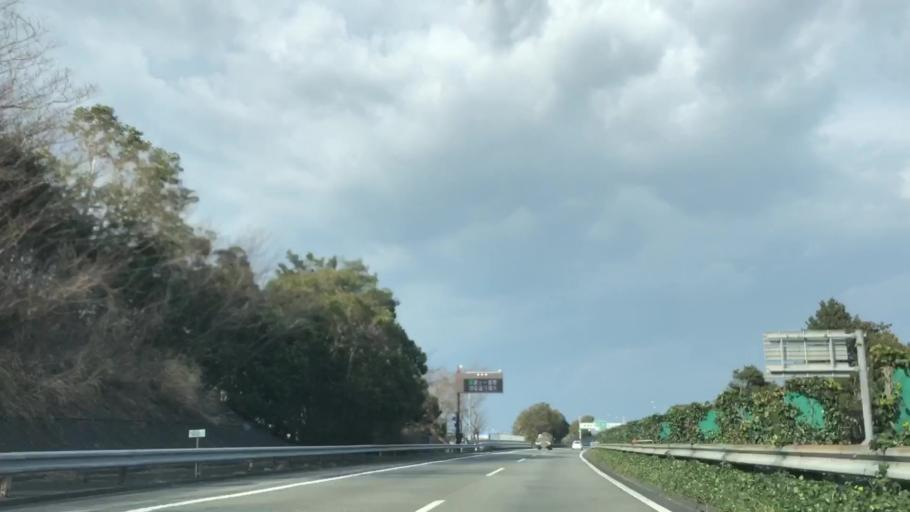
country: JP
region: Shizuoka
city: Shimada
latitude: 34.7859
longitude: 138.2306
